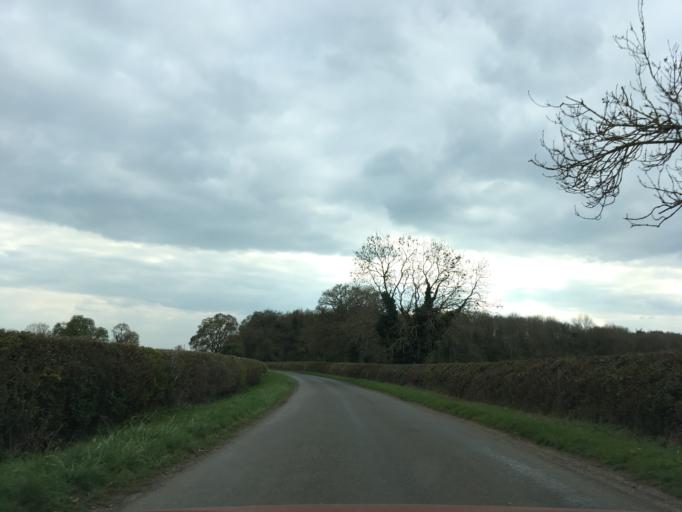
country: GB
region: England
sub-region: Oxfordshire
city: Bicester
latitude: 51.9327
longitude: -1.1427
